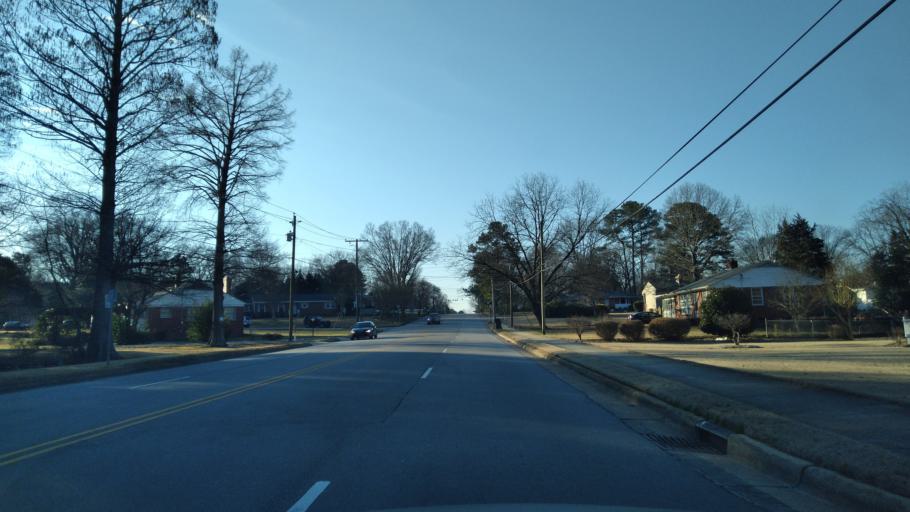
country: US
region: North Carolina
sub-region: Wake County
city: Garner
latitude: 35.7038
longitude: -78.6188
